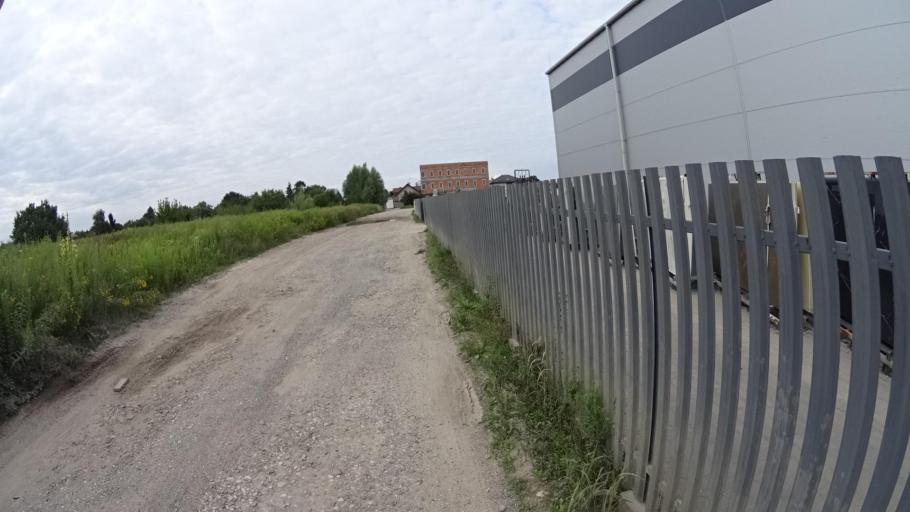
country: PL
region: Masovian Voivodeship
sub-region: Warszawa
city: Bemowo
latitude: 52.2372
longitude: 20.8822
